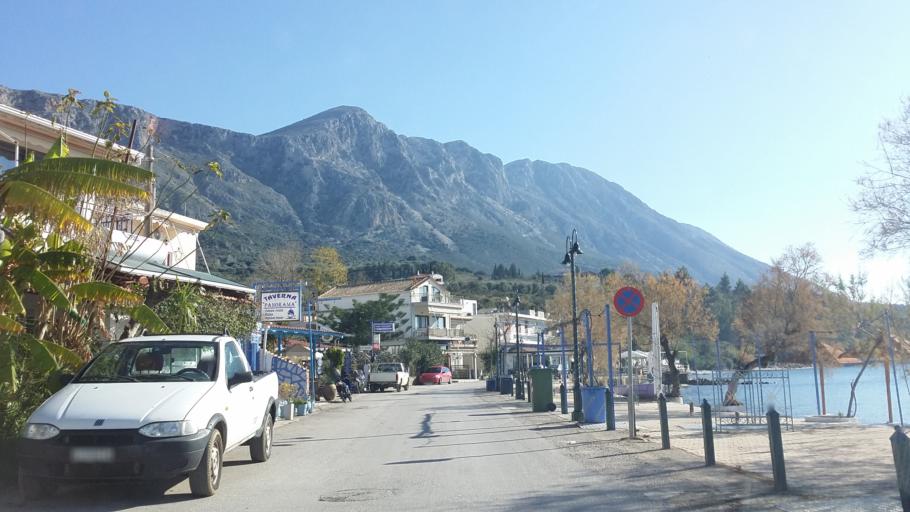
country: GR
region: West Greece
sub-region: Nomos Aitolias kai Akarnanias
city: Palairos
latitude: 38.7801
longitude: 20.8793
